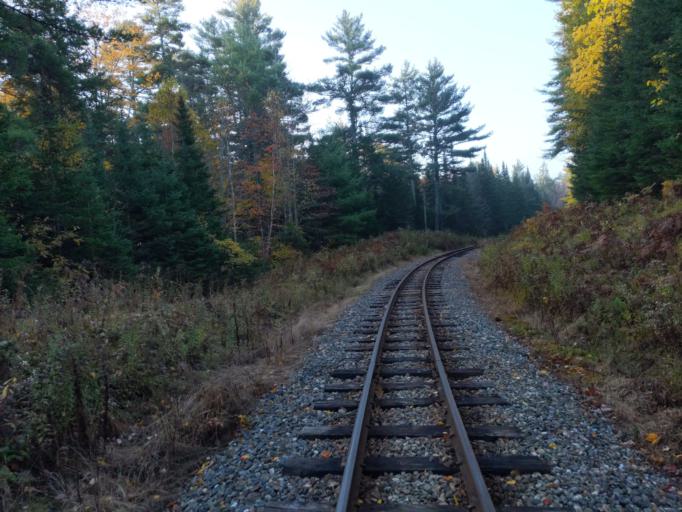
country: US
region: Maine
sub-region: Lincoln County
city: Wiscasset
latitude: 44.0641
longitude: -69.6214
